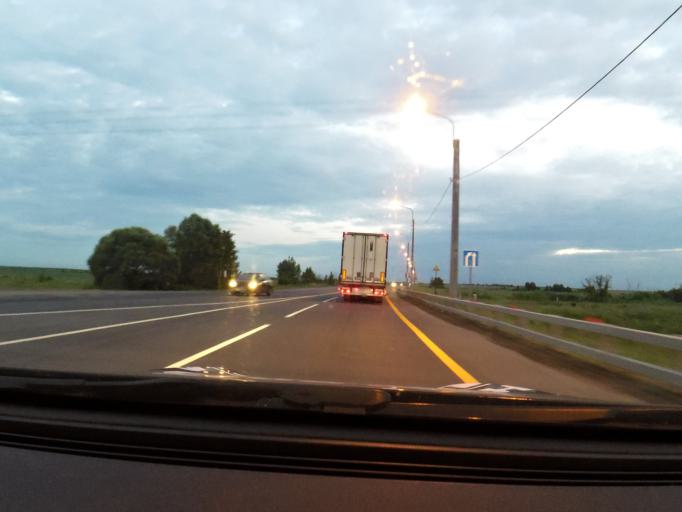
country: RU
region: Chuvashia
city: Yadrin
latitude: 56.0172
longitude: 46.2381
